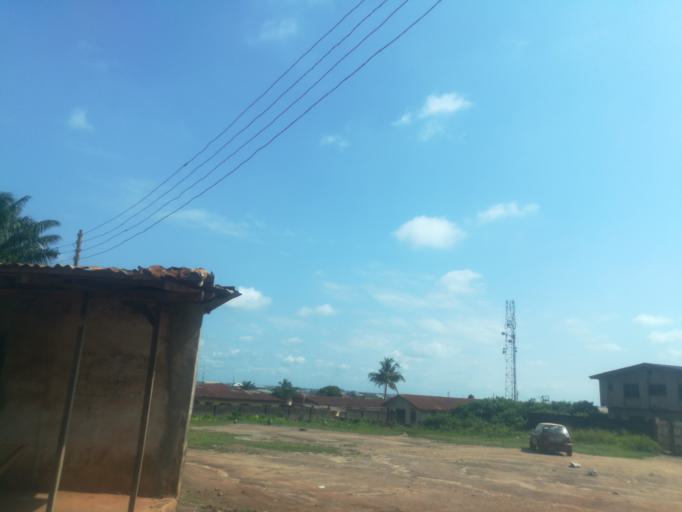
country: NG
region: Oyo
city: Egbeda
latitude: 7.4160
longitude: 3.9905
